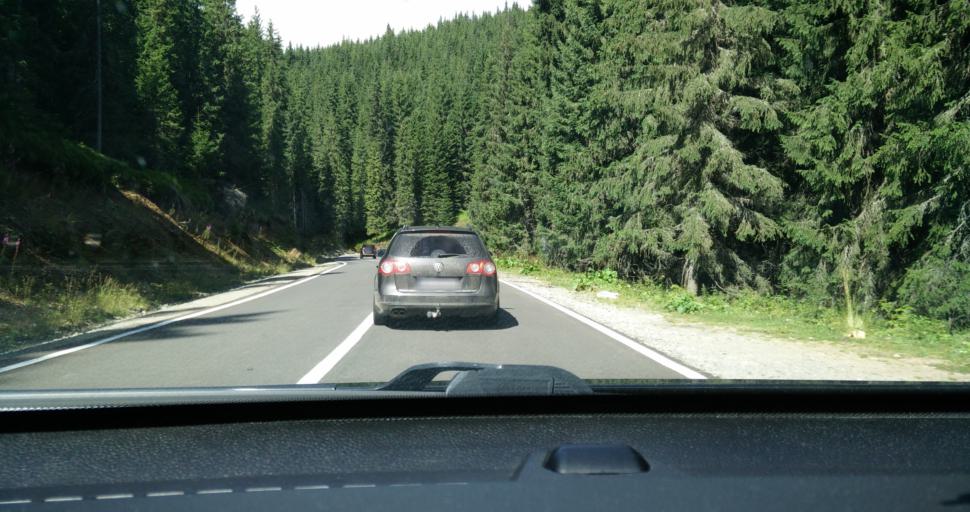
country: RO
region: Hunedoara
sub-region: Oras Petrila
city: Petrila
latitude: 45.5055
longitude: 23.6483
